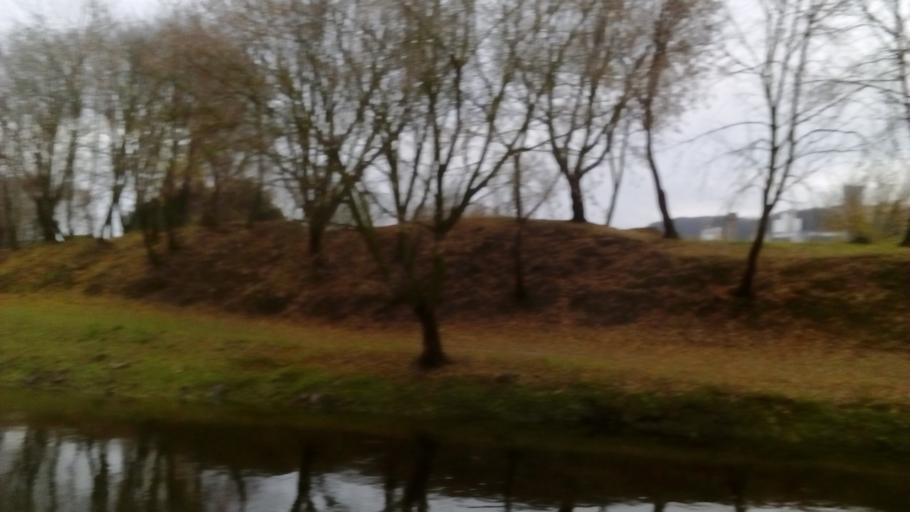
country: LT
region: Kauno apskritis
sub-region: Kaunas
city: Kaunas
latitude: 54.8940
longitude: 23.9013
